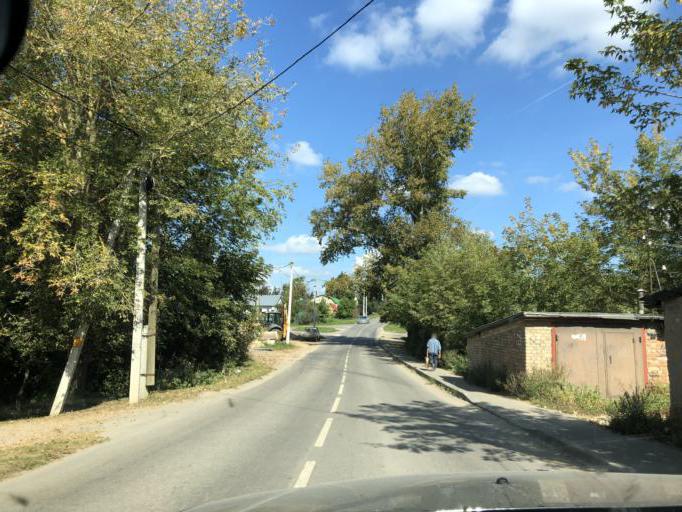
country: RU
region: Tula
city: Yasnogorsk
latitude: 54.4839
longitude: 37.6950
